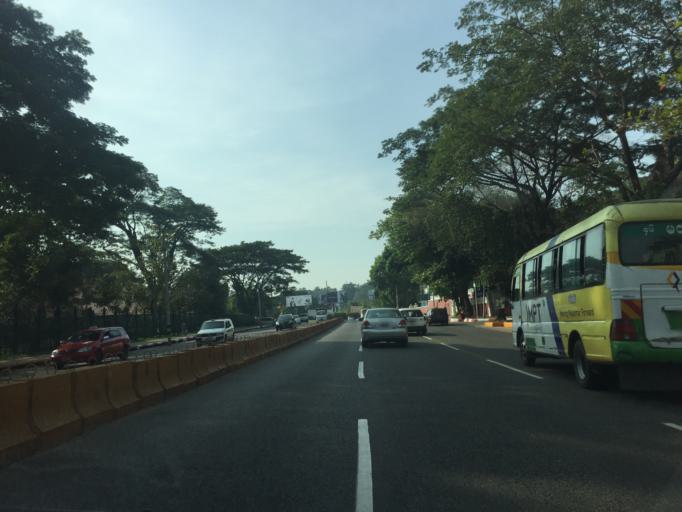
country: MM
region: Yangon
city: Yangon
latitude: 16.7975
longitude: 96.1570
